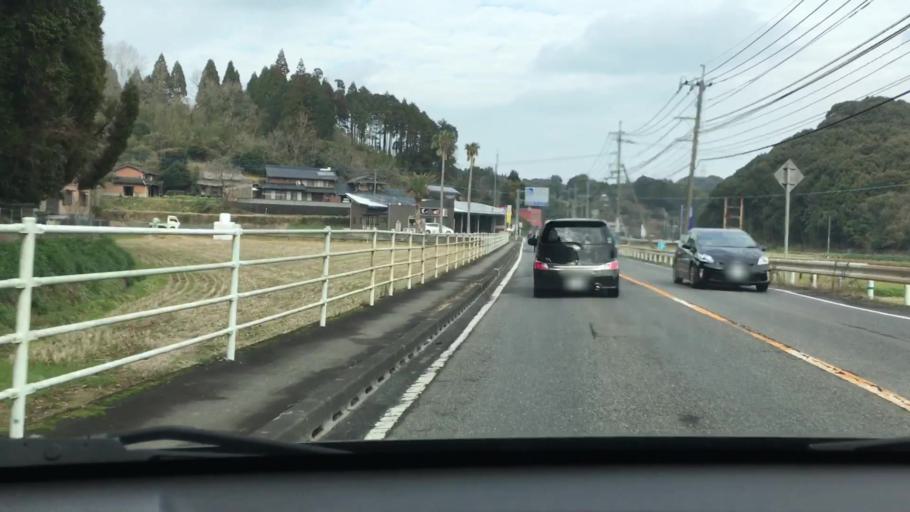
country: JP
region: Saga Prefecture
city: Imaricho-ko
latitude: 33.2982
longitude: 129.9172
